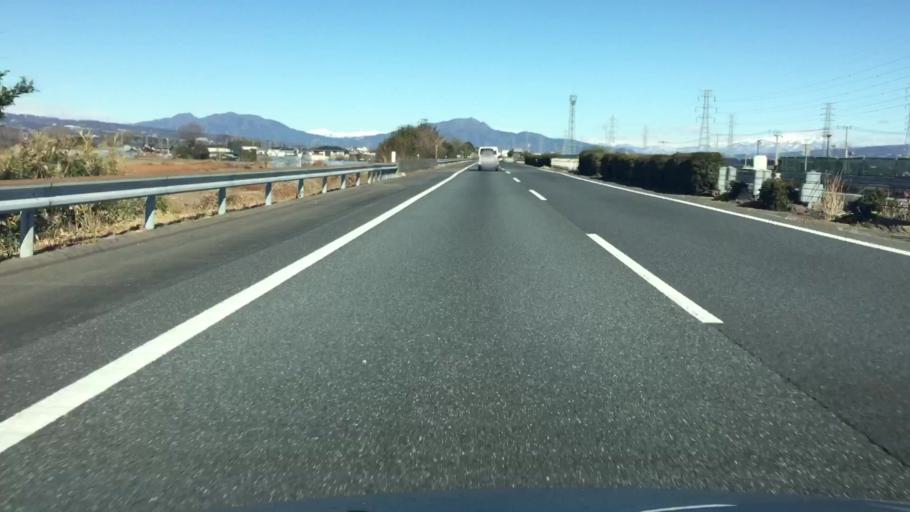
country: JP
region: Gunma
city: Maebashi-shi
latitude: 36.3914
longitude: 139.0256
